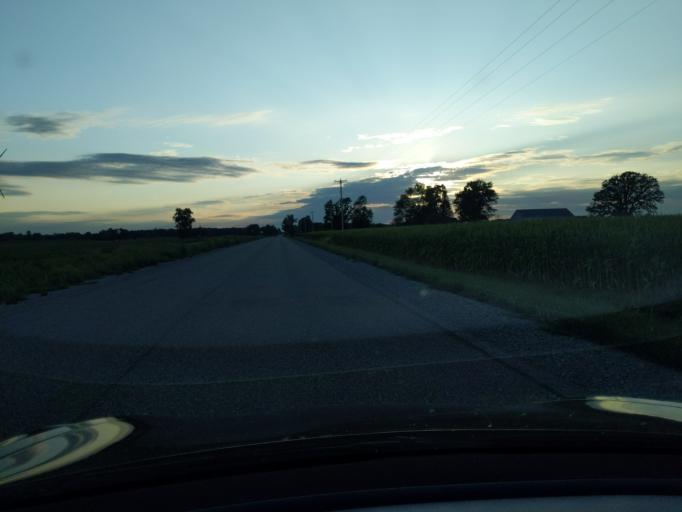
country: US
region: Michigan
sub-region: Gratiot County
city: Saint Louis
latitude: 43.3788
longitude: -84.5648
